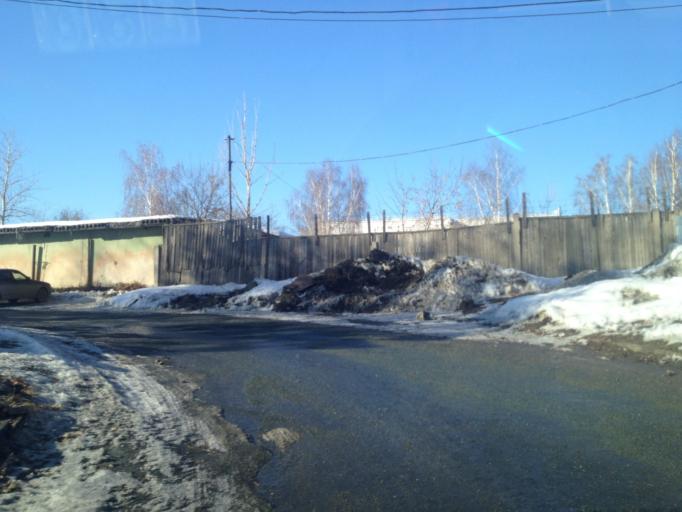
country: RU
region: Sverdlovsk
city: Yekaterinburg
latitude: 56.9117
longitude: 60.6333
